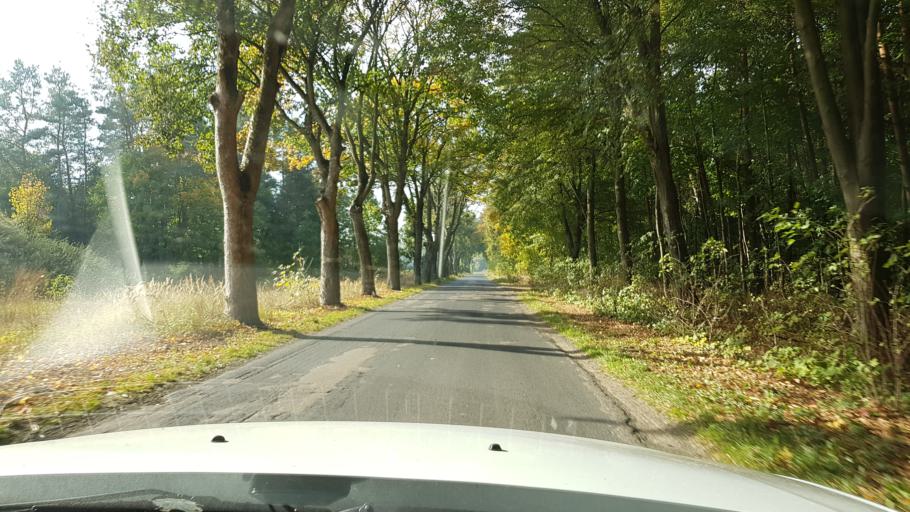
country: PL
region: West Pomeranian Voivodeship
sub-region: Powiat mysliborski
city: Barlinek
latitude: 52.9641
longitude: 15.1420
